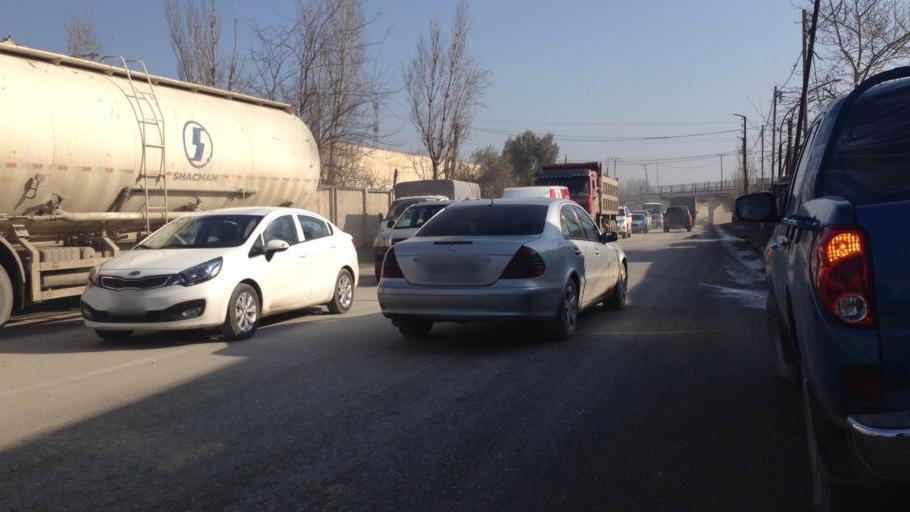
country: AZ
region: Baki
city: Binagadi
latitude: 40.4402
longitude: 49.8453
